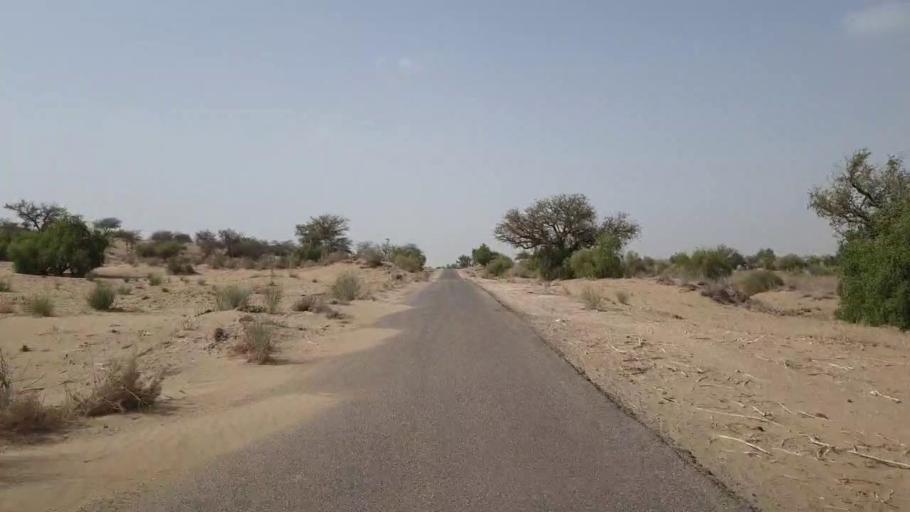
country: PK
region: Sindh
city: Mithi
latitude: 24.5916
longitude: 69.9240
